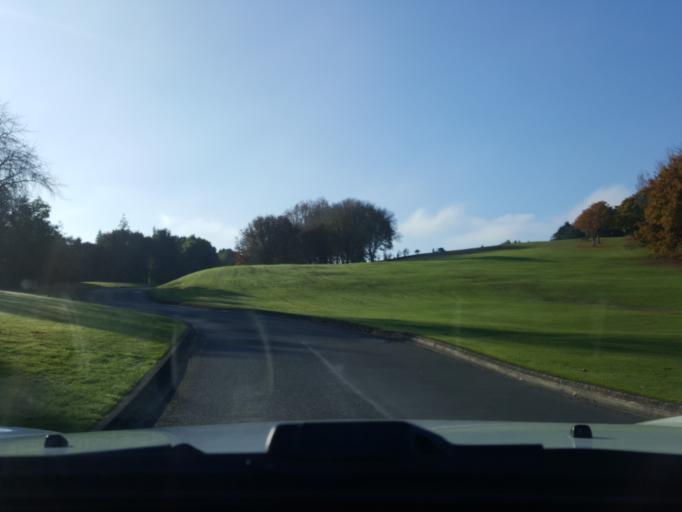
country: NZ
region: Waikato
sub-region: Hamilton City
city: Hamilton
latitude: -37.8058
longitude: 175.3049
